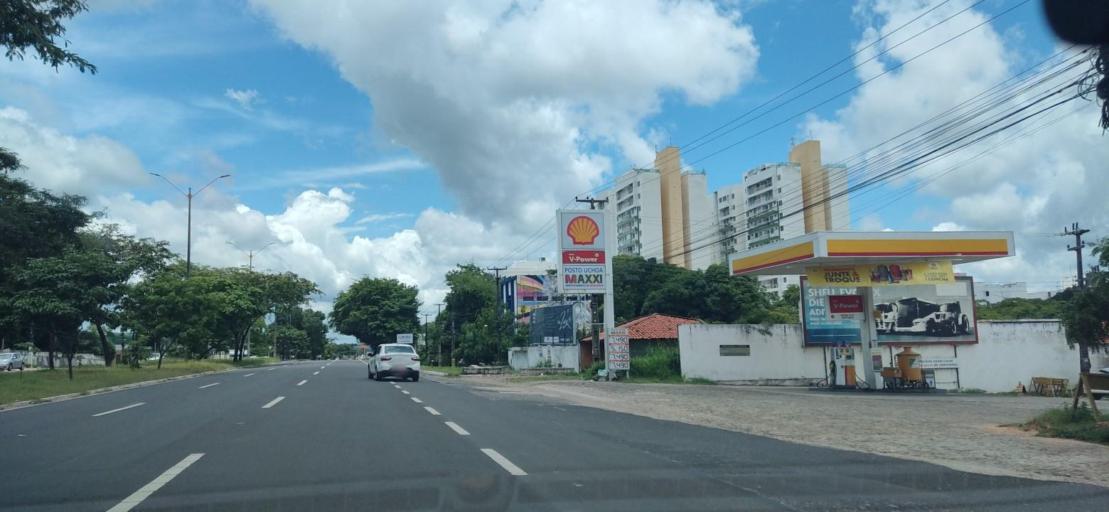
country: BR
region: Piaui
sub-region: Teresina
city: Teresina
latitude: -5.0815
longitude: -42.7656
